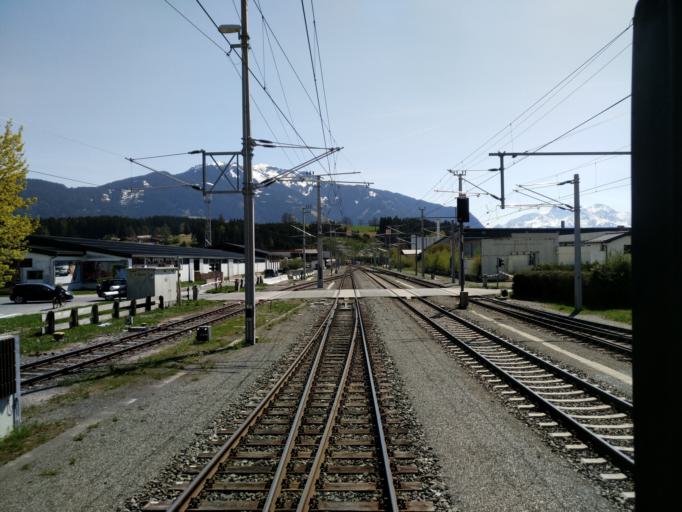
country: AT
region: Salzburg
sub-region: Politischer Bezirk Zell am See
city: Saalfelden am Steinernen Meer
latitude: 47.4244
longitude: 12.8306
